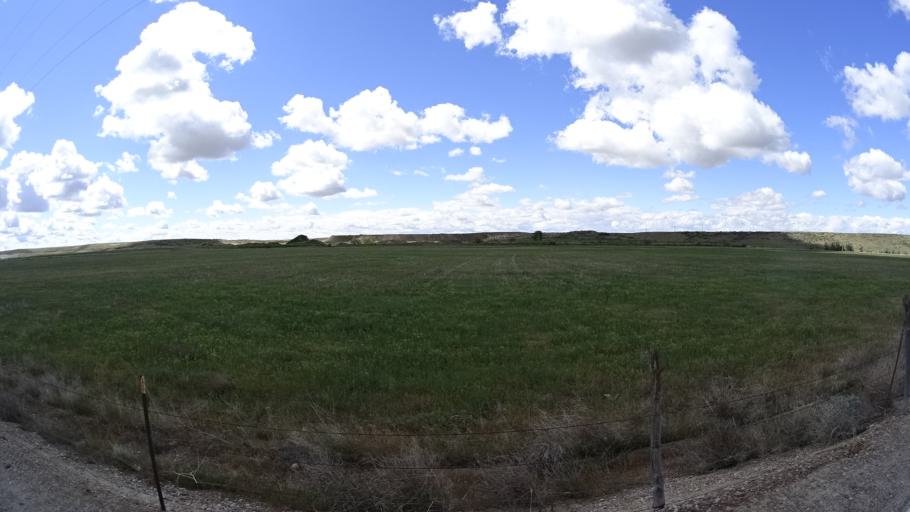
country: US
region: Idaho
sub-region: Ada County
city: Garden City
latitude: 43.4920
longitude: -116.2701
